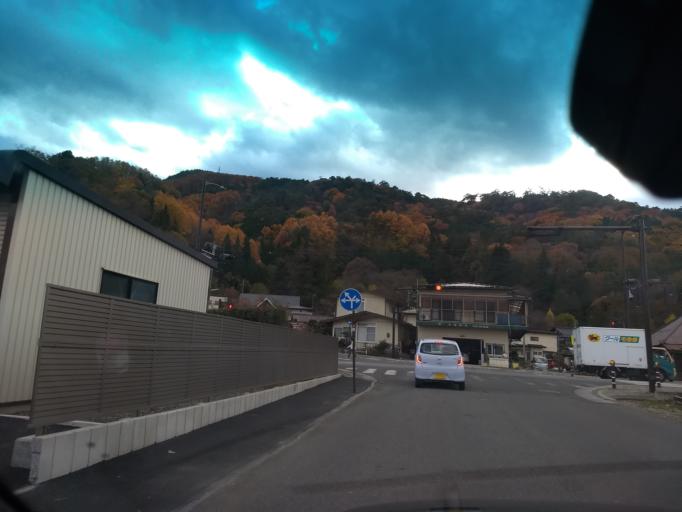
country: JP
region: Nagano
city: Chino
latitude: 35.9981
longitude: 138.1235
